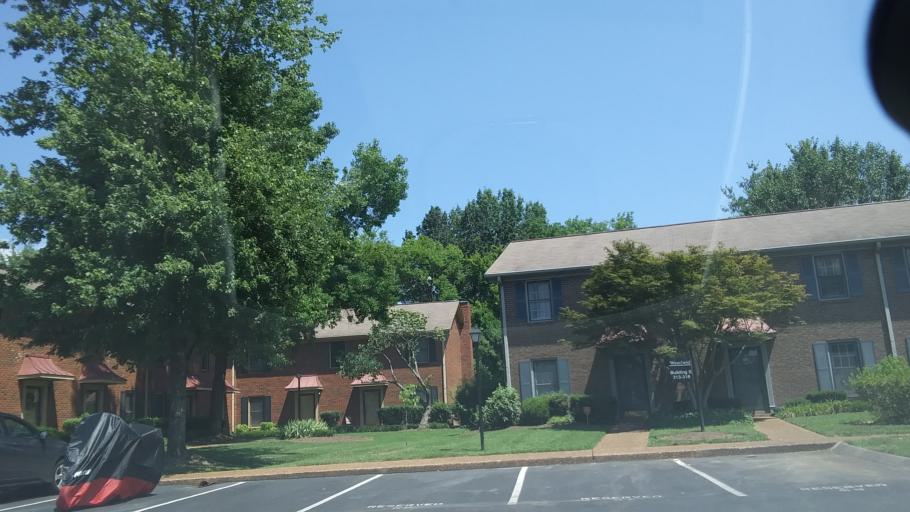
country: US
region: Tennessee
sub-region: Davidson County
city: Belle Meade
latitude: 36.0849
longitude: -86.9461
